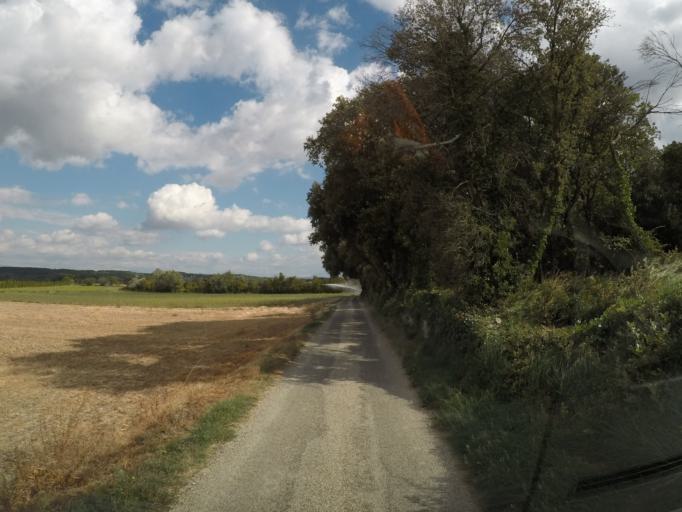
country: FR
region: Rhone-Alpes
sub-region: Departement de la Drome
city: Saint-Restitut
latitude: 44.3026
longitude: 4.7982
